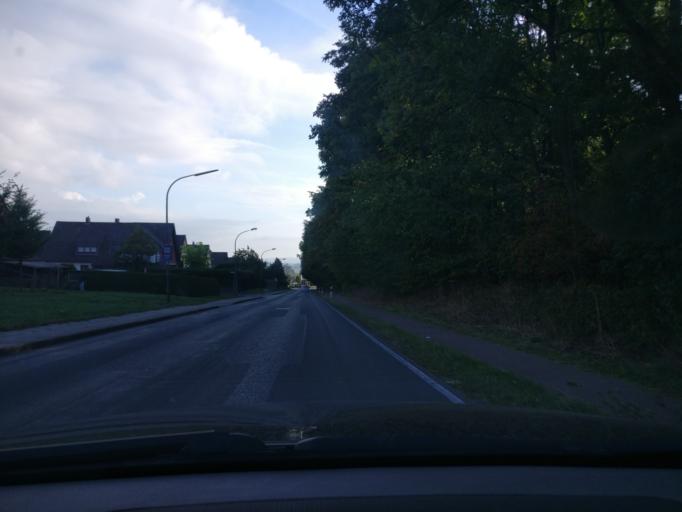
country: DE
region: Lower Saxony
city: Melle
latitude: 52.1884
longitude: 8.3488
